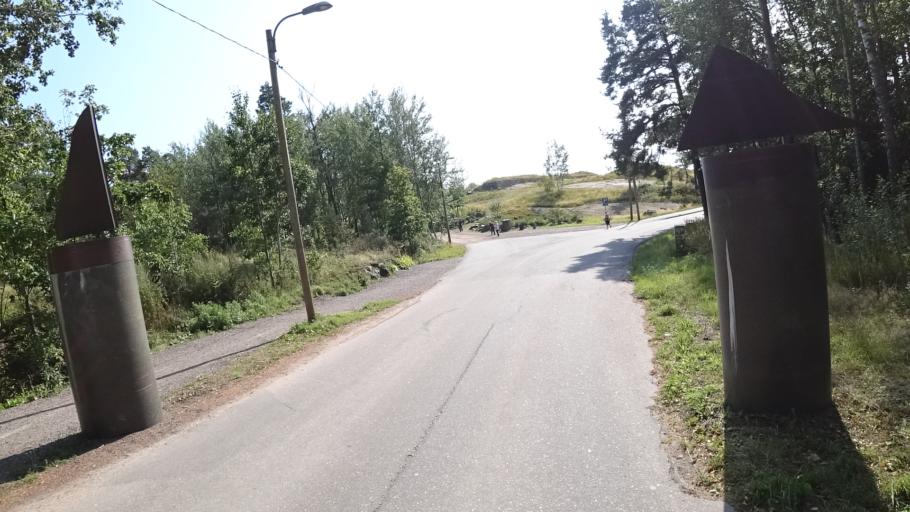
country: FI
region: Kymenlaakso
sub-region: Kotka-Hamina
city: Kotka
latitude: 60.4521
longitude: 26.9373
